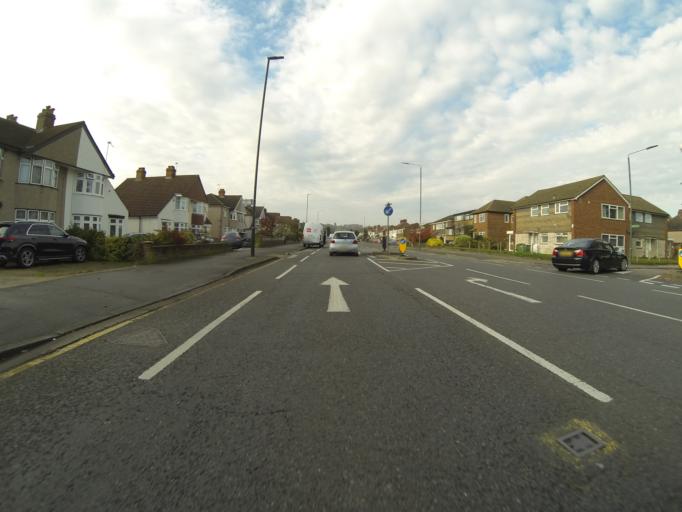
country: GB
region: England
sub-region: Greater London
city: Welling
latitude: 51.4649
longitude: 0.0922
